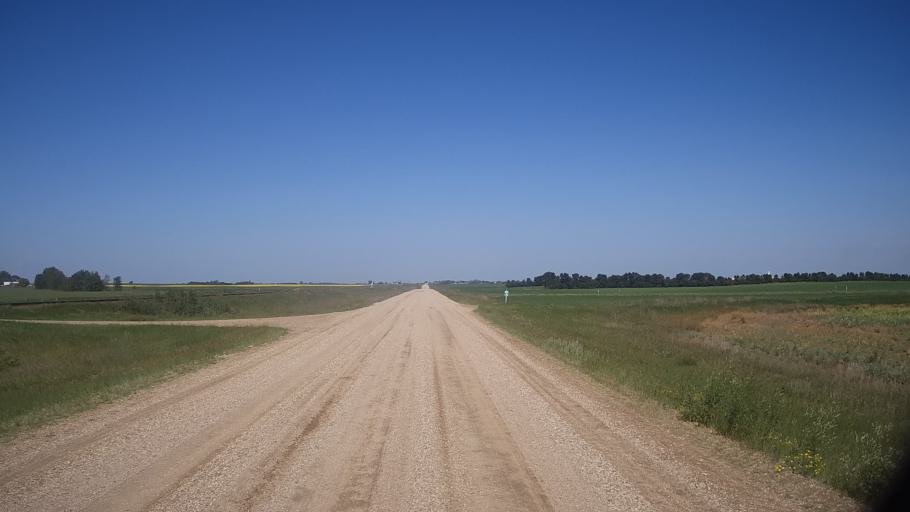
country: CA
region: Saskatchewan
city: Watrous
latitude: 51.8744
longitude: -106.0033
